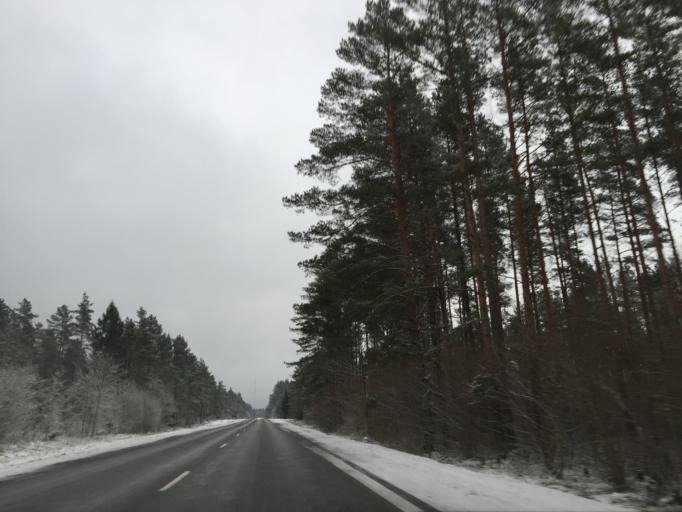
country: EE
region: Laeaene
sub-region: Lihula vald
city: Lihula
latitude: 58.6099
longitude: 23.9381
